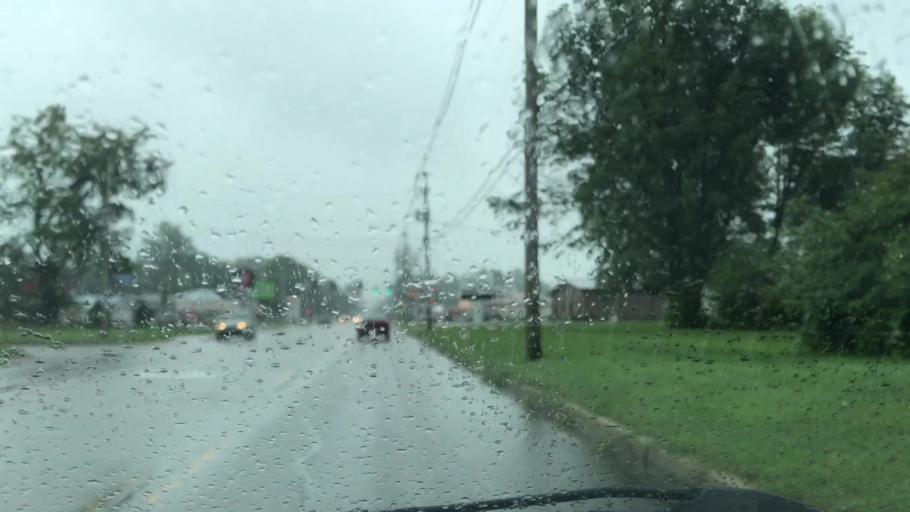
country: US
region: Indiana
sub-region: Boone County
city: Lebanon
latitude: 40.0628
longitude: -86.4721
